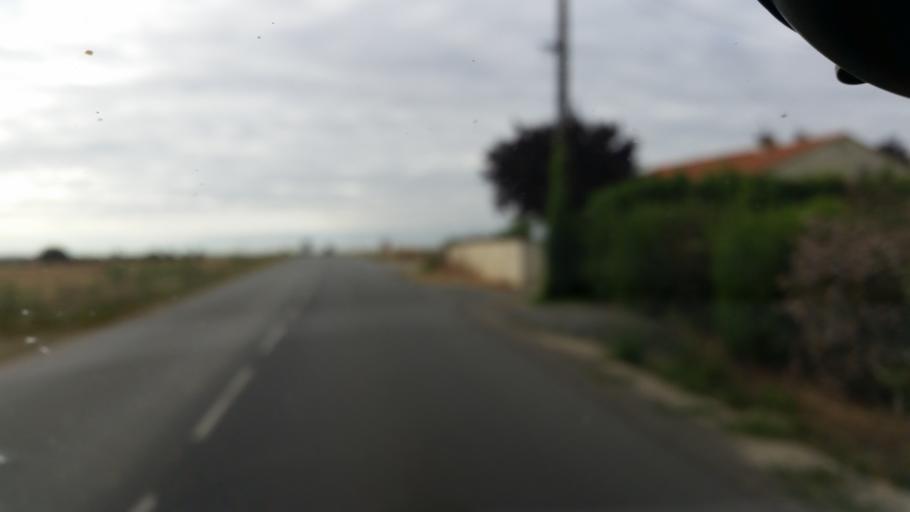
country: FR
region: Poitou-Charentes
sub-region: Departement de la Charente-Maritime
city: Marans
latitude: 46.3009
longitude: -0.9818
